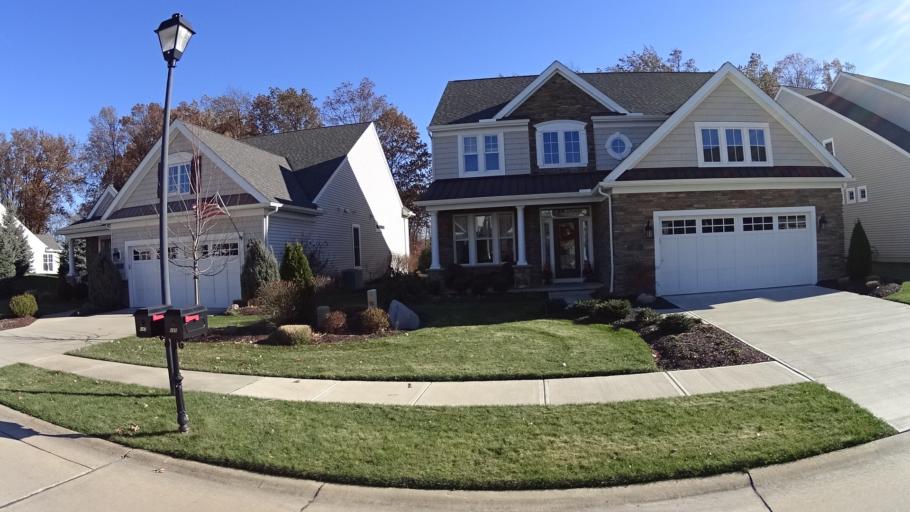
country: US
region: Ohio
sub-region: Lorain County
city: Avon Center
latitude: 41.4817
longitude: -82.0089
